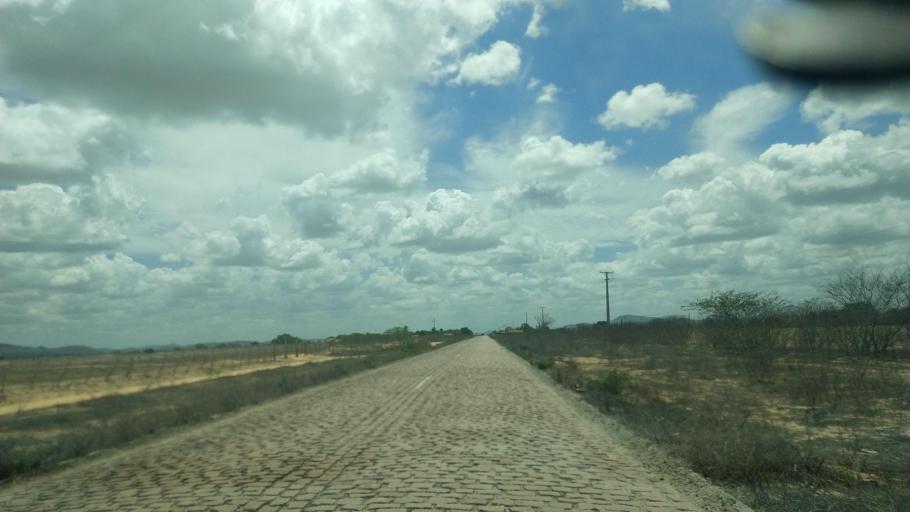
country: BR
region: Rio Grande do Norte
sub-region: Sao Paulo Do Potengi
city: Sao Paulo do Potengi
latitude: -5.9749
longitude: -35.8552
